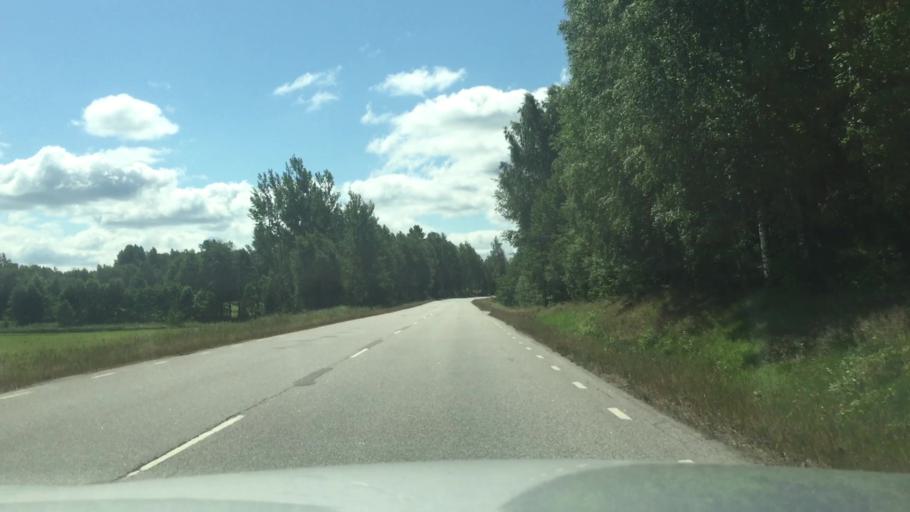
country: SE
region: Vaestra Goetaland
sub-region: Karlsborgs Kommun
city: Molltorp
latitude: 58.6281
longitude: 14.3884
